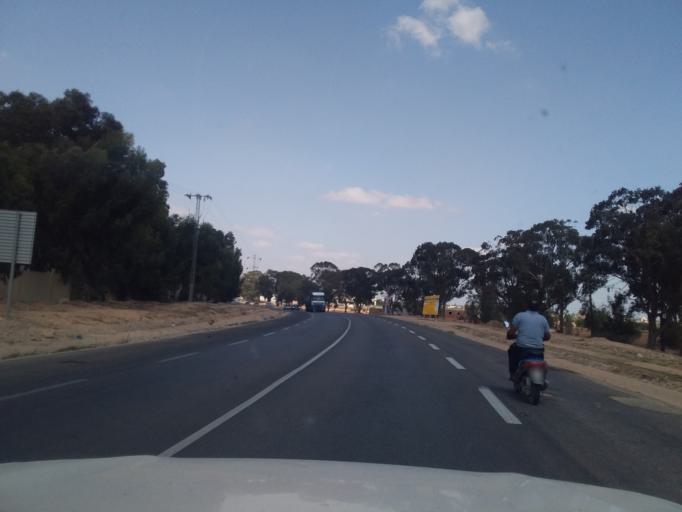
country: TN
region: Madanin
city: Medenine
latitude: 33.6007
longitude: 10.3086
